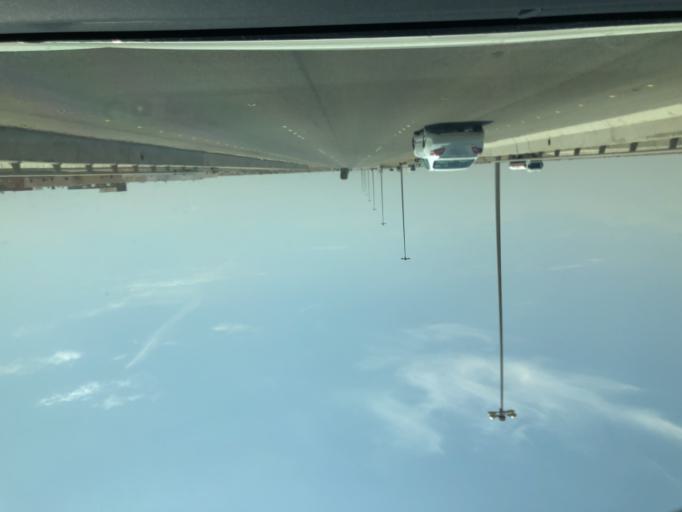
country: SA
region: Makkah
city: Rabigh
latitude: 22.2603
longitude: 39.1196
